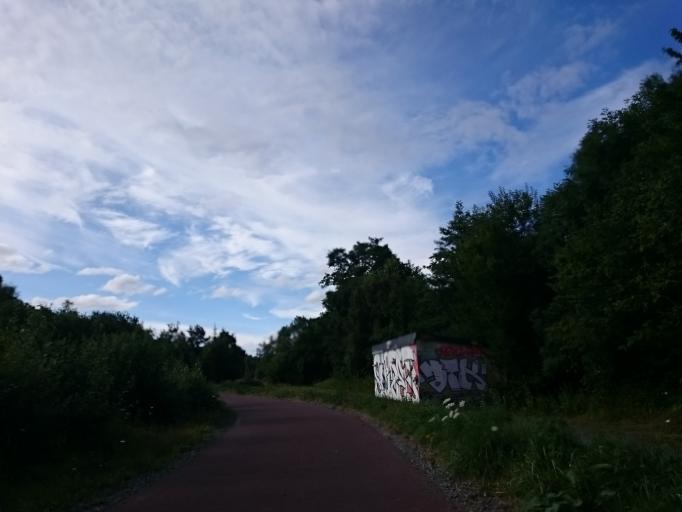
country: FR
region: Lower Normandy
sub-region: Departement du Calvados
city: May-sur-Orne
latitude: 49.1050
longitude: -0.3847
